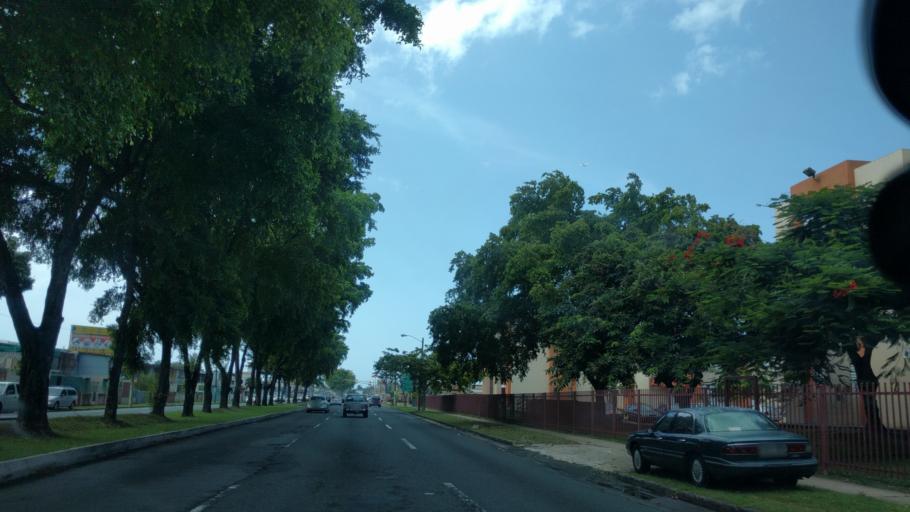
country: PR
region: Bayamon
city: Bayamon
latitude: 18.4139
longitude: -66.1610
